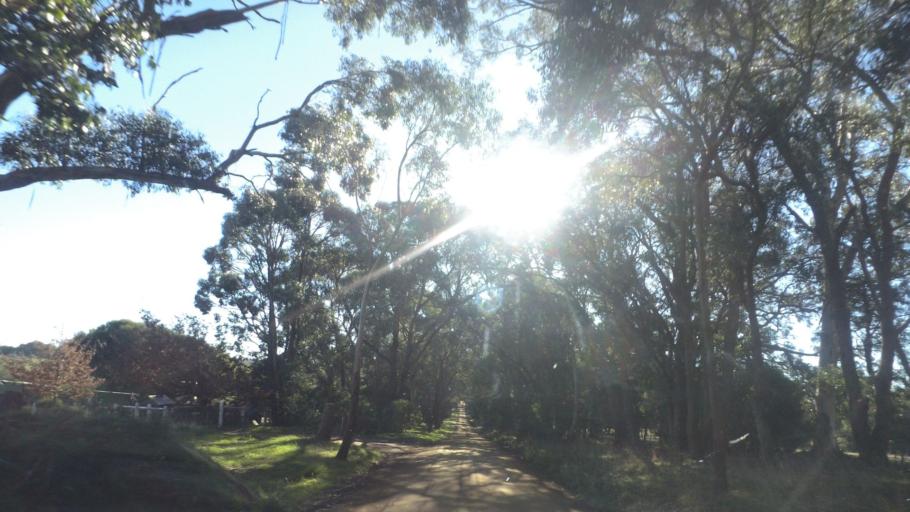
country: AU
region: Victoria
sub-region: Mount Alexander
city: Castlemaine
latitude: -37.2971
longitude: 144.3332
